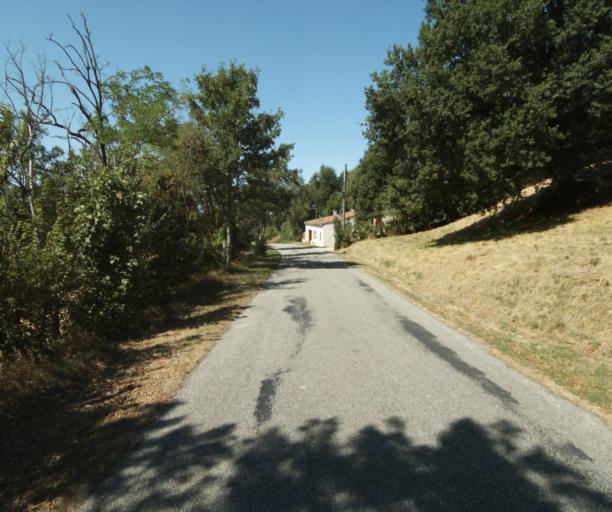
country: FR
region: Midi-Pyrenees
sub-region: Departement de la Haute-Garonne
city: Saint-Felix-Lauragais
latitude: 43.4920
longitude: 1.8974
